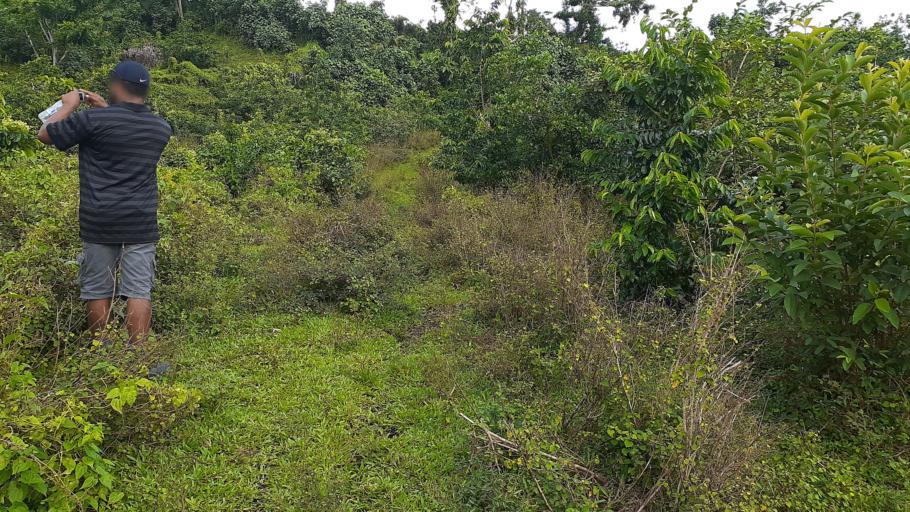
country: VU
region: Penama
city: Saratamata
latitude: -15.9438
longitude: 168.1936
